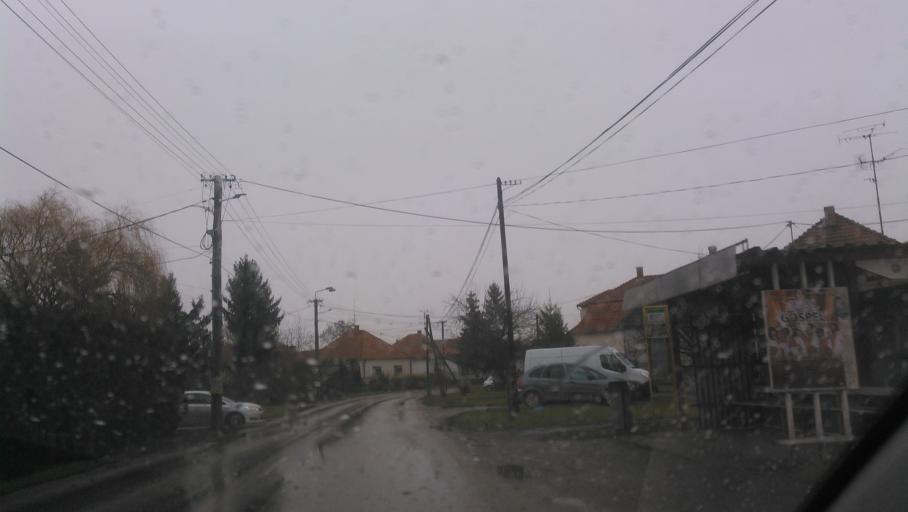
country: SK
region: Nitriansky
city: Kolarovo
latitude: 47.9261
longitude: 17.9821
